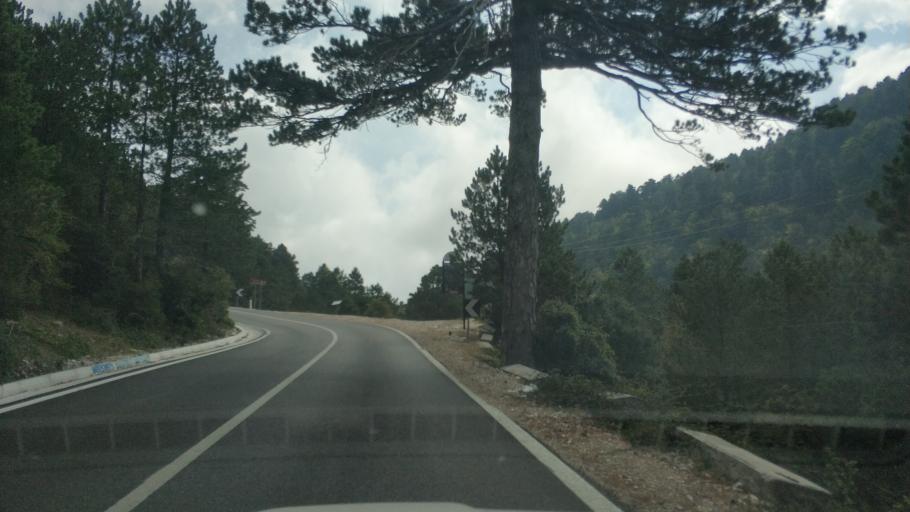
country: AL
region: Vlore
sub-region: Rrethi i Vlores
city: Vranisht
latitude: 40.2015
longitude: 19.5894
